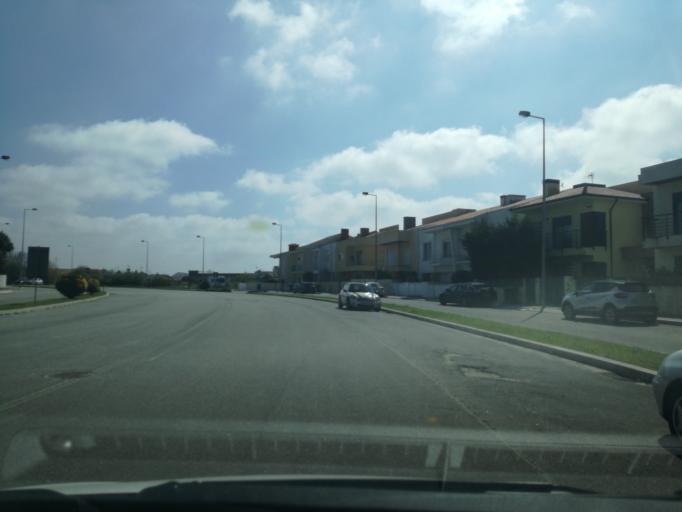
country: PT
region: Porto
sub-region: Matosinhos
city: Santa Cruz do Bispo
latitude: 41.2482
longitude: -8.6759
